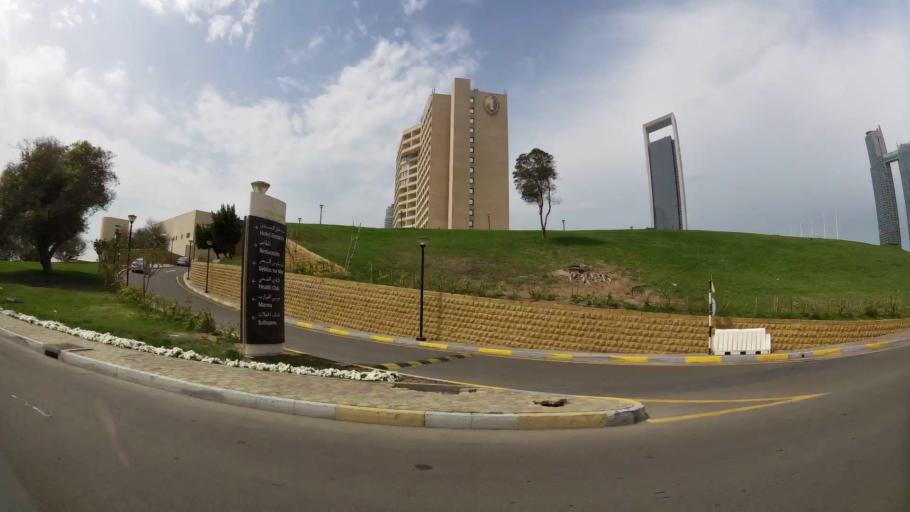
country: AE
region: Abu Dhabi
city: Abu Dhabi
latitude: 24.4574
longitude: 54.3301
